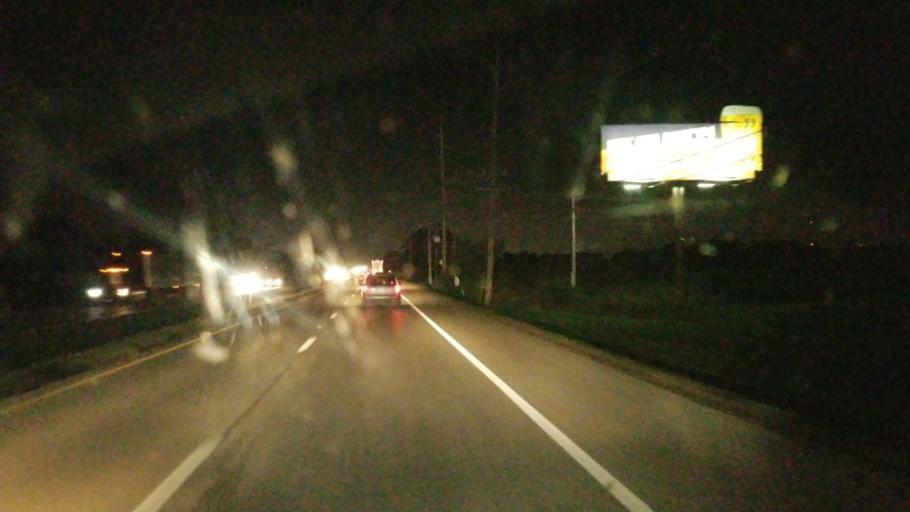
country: US
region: Ohio
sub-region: Franklin County
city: Obetz
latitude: 39.8428
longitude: -83.0009
